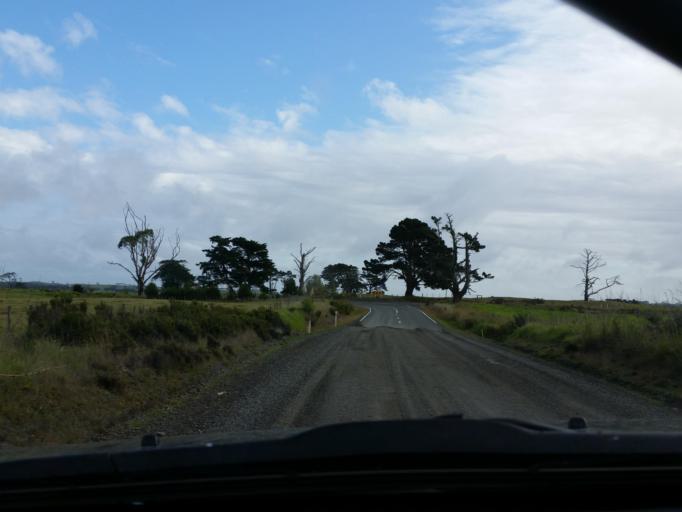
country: NZ
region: Northland
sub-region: Kaipara District
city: Dargaville
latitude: -36.0272
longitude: 173.8927
